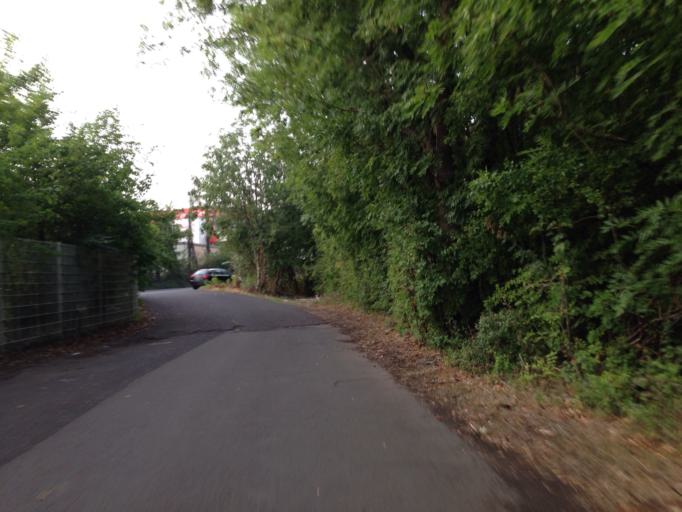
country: DE
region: Hesse
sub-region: Regierungsbezirk Giessen
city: Heuchelheim
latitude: 50.5711
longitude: 8.6526
